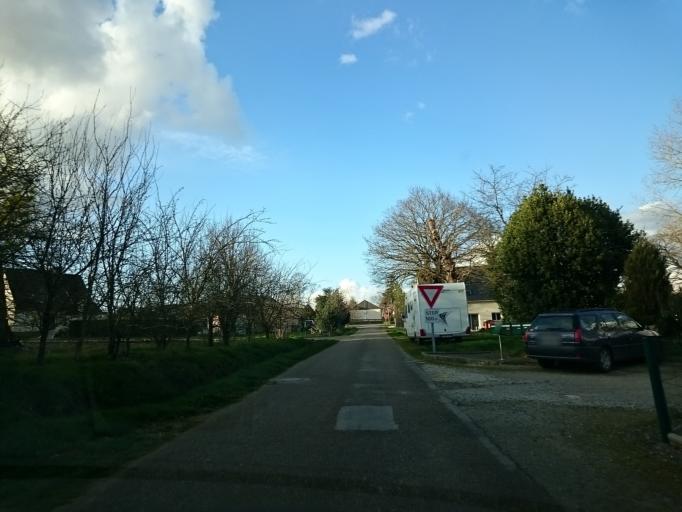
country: FR
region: Brittany
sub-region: Departement d'Ille-et-Vilaine
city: Crevin
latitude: 47.9348
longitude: -1.6549
